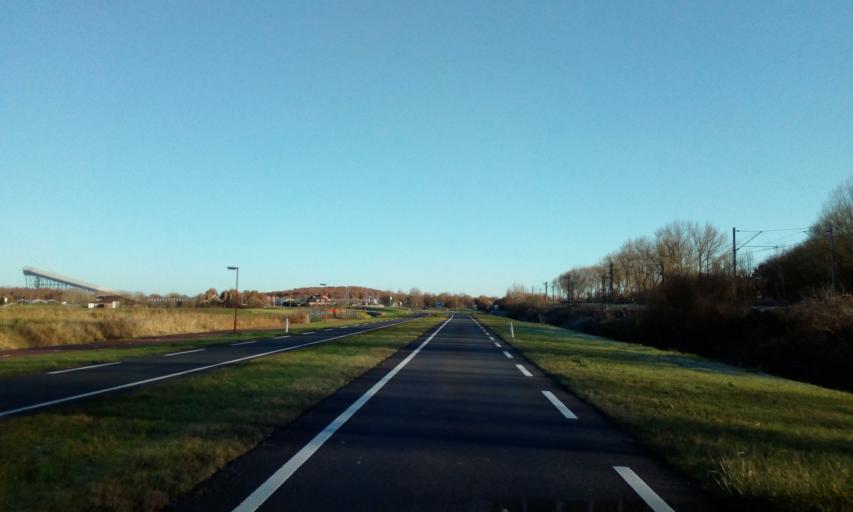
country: NL
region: South Holland
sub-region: Gemeente Pijnacker-Nootdorp
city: Pijnacker
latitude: 52.0610
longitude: 4.4468
